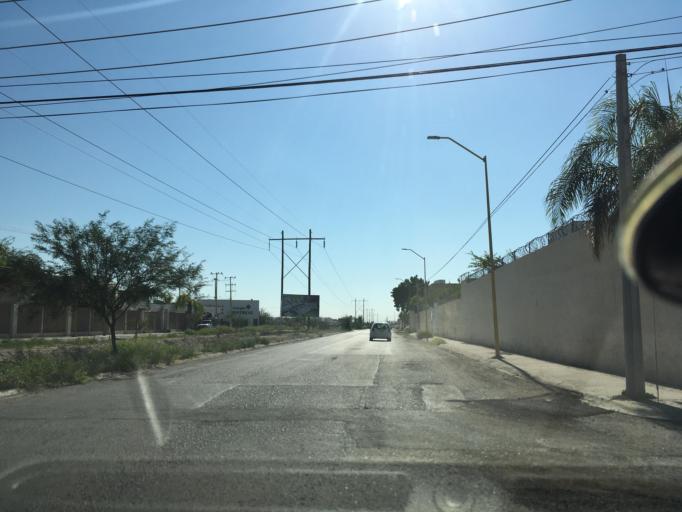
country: MX
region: Coahuila
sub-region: Torreon
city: Fraccionamiento la Noria
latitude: 25.5748
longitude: -103.3753
